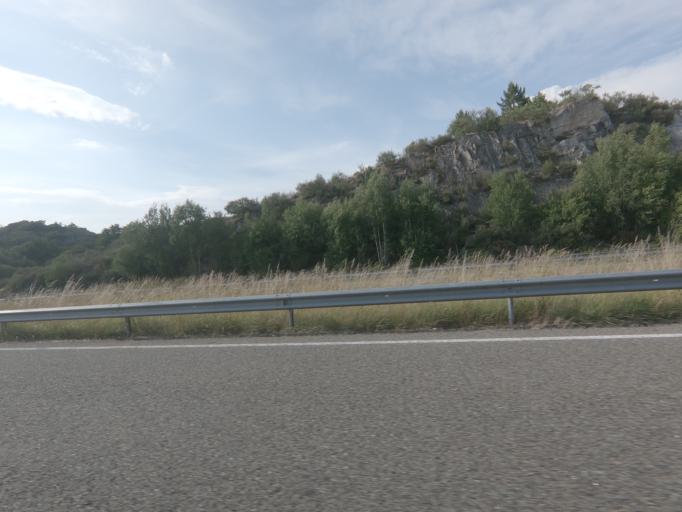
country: ES
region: Galicia
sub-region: Provincia de Ourense
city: Xinzo de Limia
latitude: 42.0644
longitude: -7.6941
